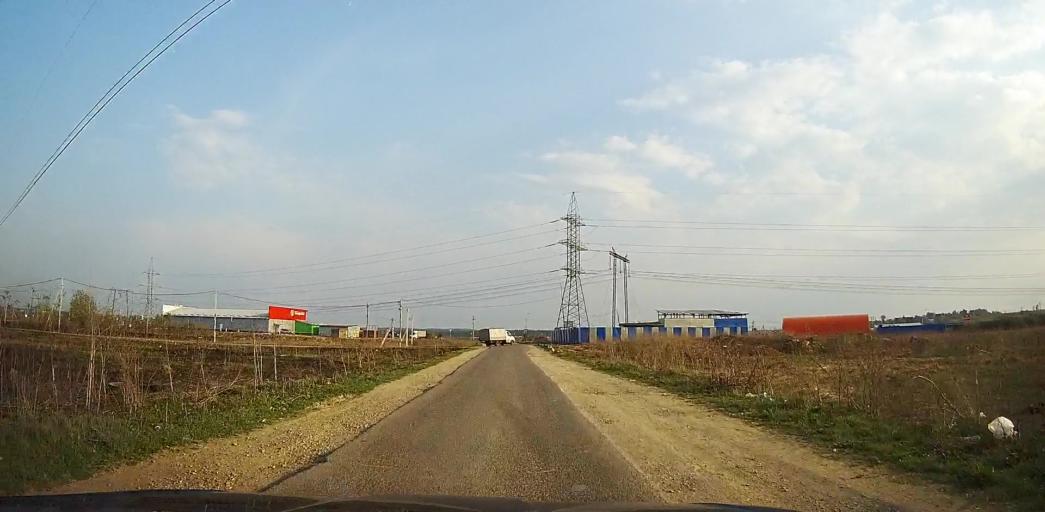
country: RU
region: Moskovskaya
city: Andreyevskoye
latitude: 55.5374
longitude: 37.9699
